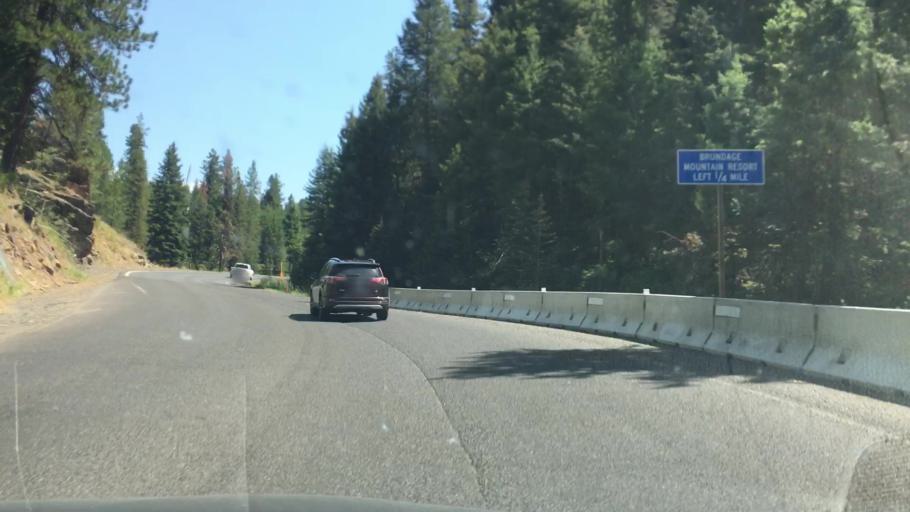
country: US
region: Idaho
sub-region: Valley County
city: McCall
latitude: 44.9610
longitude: -116.1737
